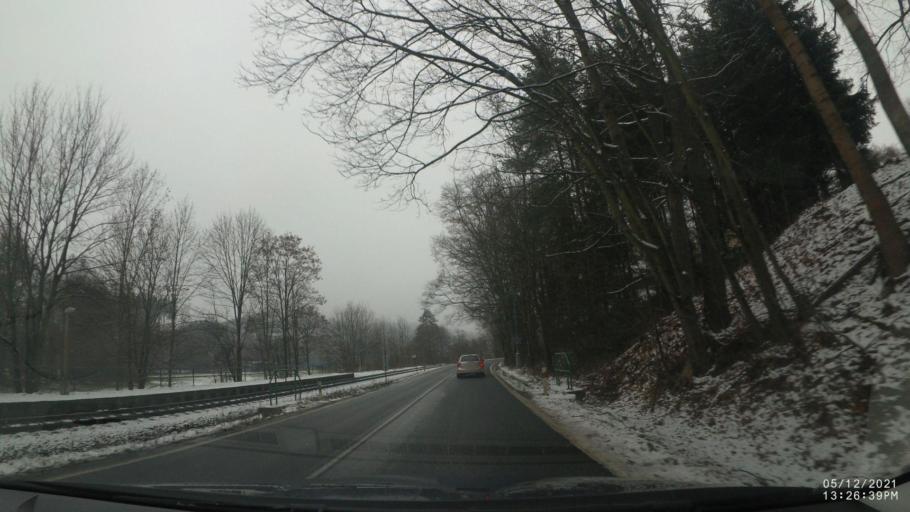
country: CZ
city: Hronov
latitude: 50.4905
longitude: 16.1867
